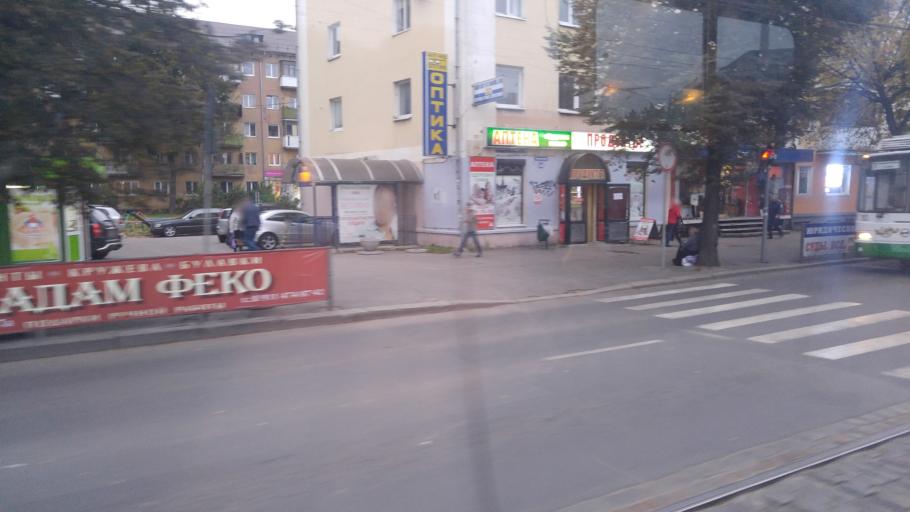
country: RU
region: Kaliningrad
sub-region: Gorod Kaliningrad
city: Kaliningrad
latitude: 54.7167
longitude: 20.5028
